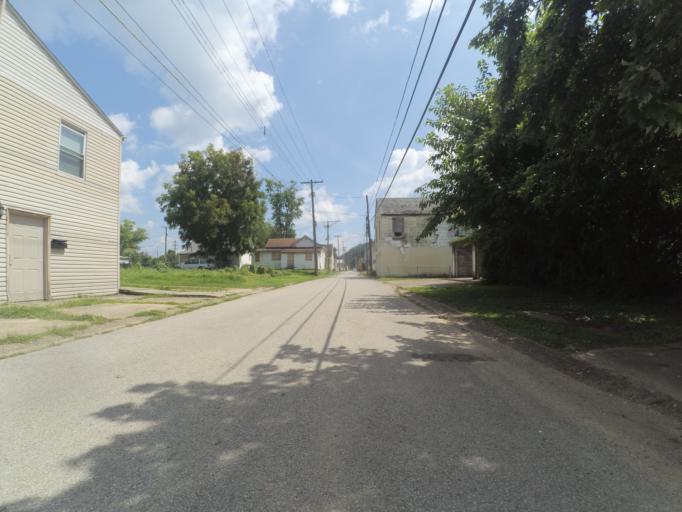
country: US
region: West Virginia
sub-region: Cabell County
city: Huntington
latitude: 38.4191
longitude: -82.4150
